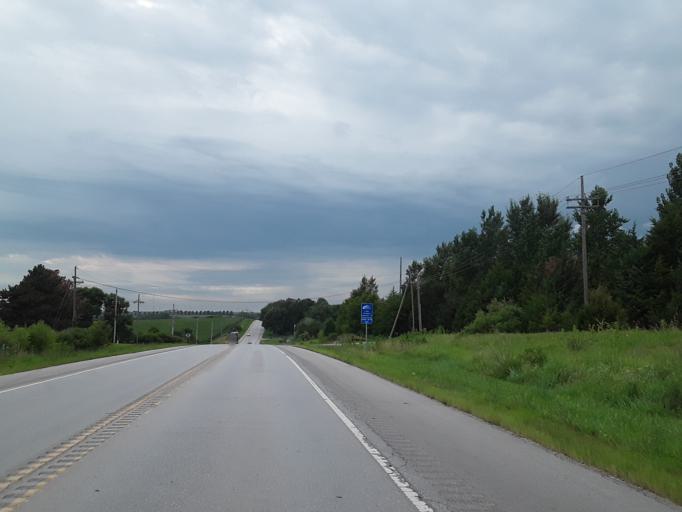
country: US
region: Nebraska
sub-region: Saunders County
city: Yutan
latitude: 41.2339
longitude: -96.3754
